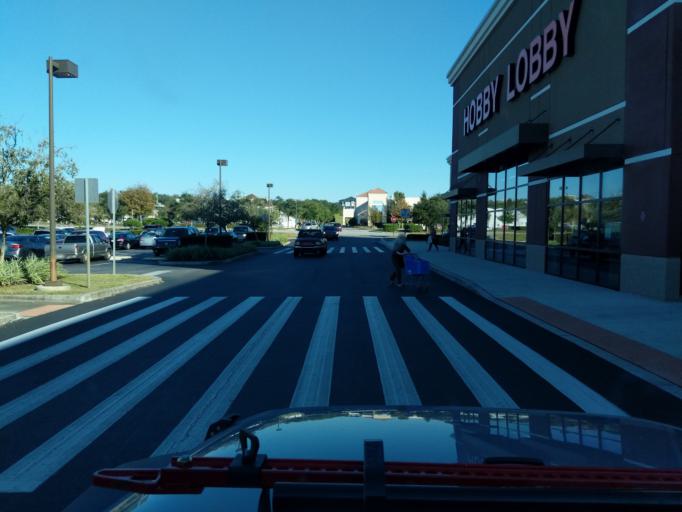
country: US
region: Florida
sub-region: Lake County
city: Minneola
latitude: 28.5444
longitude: -81.7329
